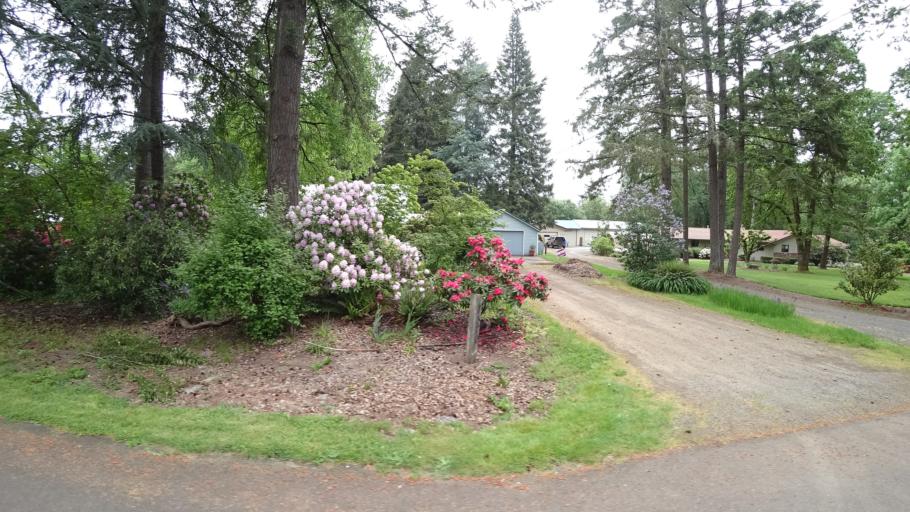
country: US
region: Oregon
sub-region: Washington County
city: Rockcreek
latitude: 45.5744
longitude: -122.8977
